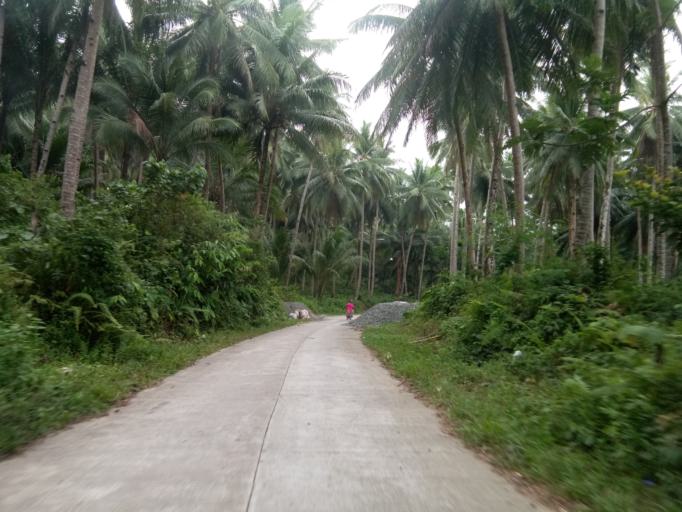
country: PH
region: Caraga
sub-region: Province of Surigao del Norte
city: Tubod
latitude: 9.5671
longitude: 125.5665
